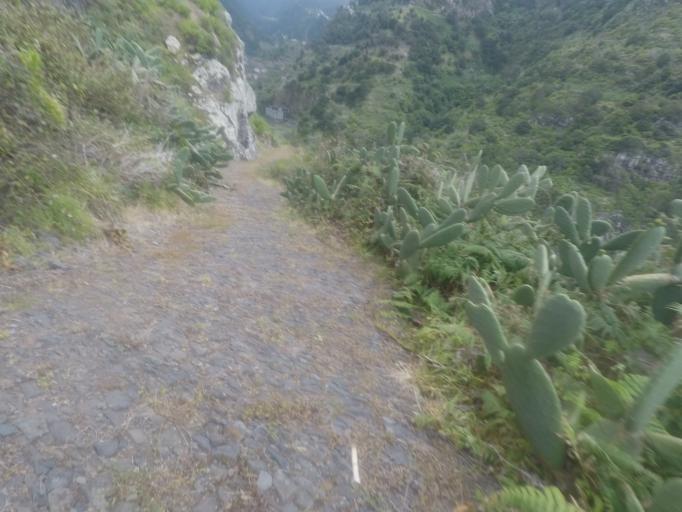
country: PT
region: Madeira
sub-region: Santana
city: Santana
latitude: 32.8287
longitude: -16.8960
